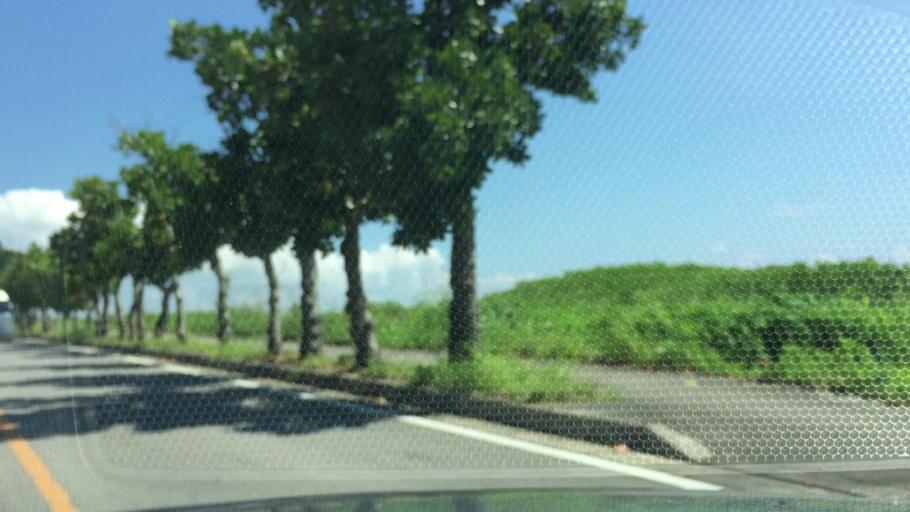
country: JP
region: Okinawa
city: Ishigaki
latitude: 24.3637
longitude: 124.2468
